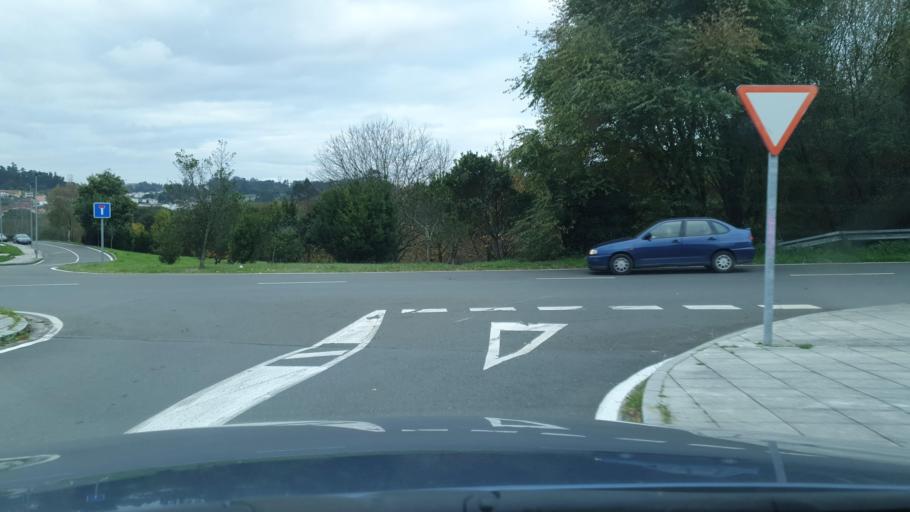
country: ES
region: Galicia
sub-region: Provincia da Coruna
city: Santiago de Compostela
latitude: 42.8662
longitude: -8.5606
